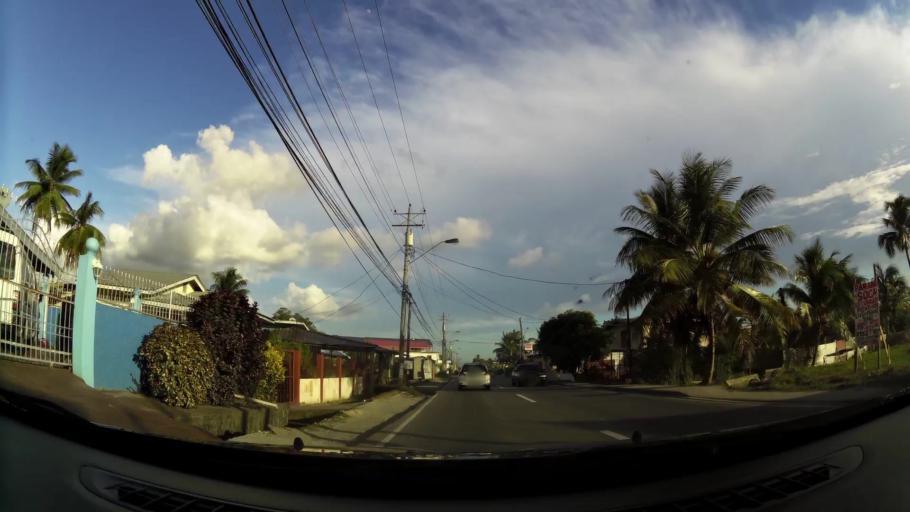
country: TT
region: Tunapuna/Piarco
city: Arouca
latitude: 10.5885
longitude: -61.3616
